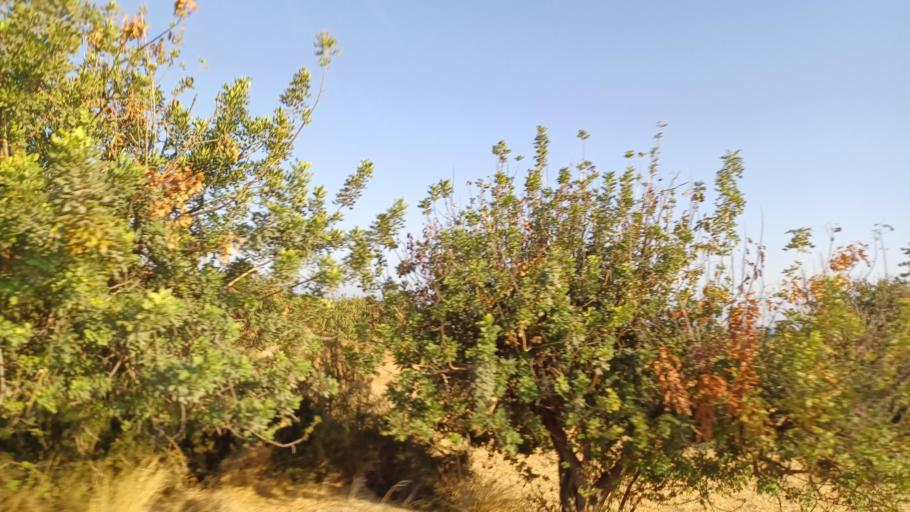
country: CY
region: Pafos
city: Polis
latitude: 35.0217
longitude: 32.3960
